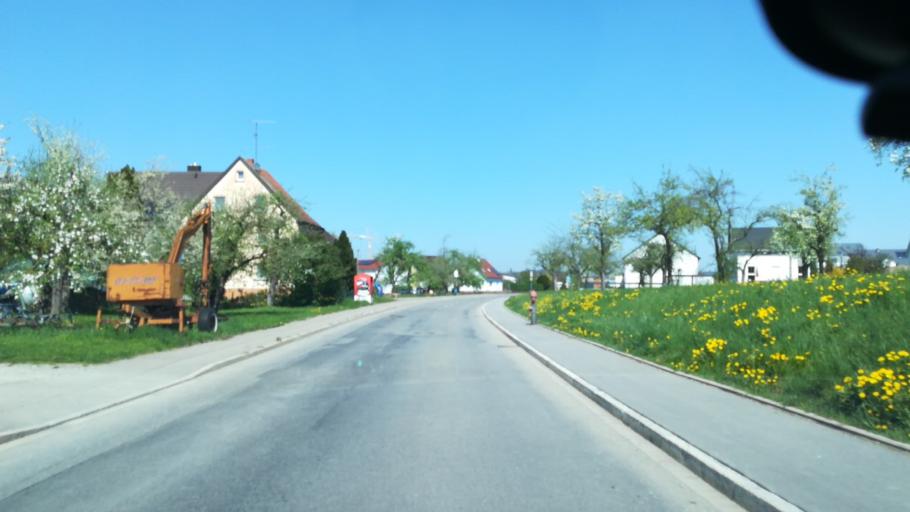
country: DE
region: Baden-Wuerttemberg
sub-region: Freiburg Region
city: Muhlhausen-Ehingen
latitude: 47.7930
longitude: 8.8404
